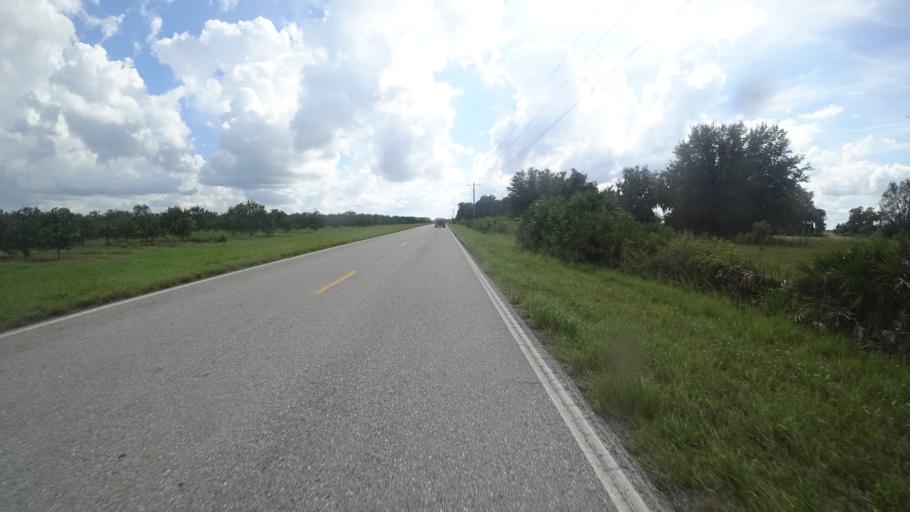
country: US
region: Florida
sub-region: Hillsborough County
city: Wimauma
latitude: 27.5804
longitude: -82.1042
